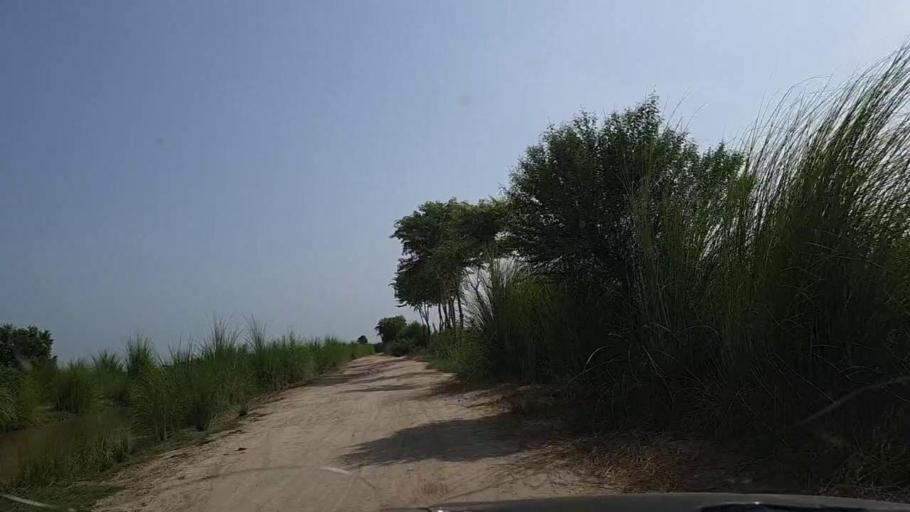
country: PK
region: Sindh
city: Ghotki
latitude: 28.0594
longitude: 69.3806
